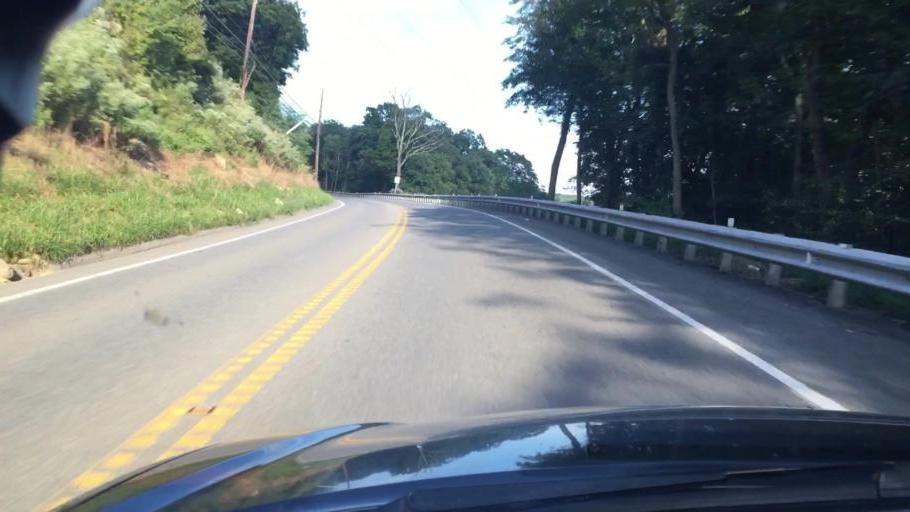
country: US
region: Pennsylvania
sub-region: Carbon County
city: Jim Thorpe
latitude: 40.8880
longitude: -75.7119
